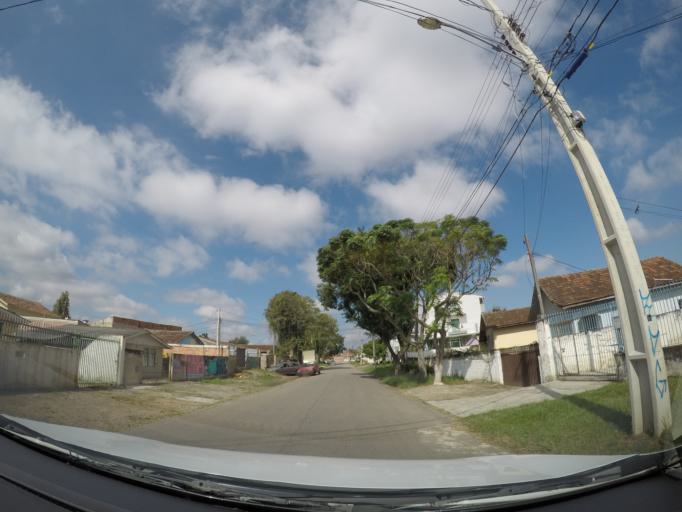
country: BR
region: Parana
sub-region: Sao Jose Dos Pinhais
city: Sao Jose dos Pinhais
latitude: -25.4949
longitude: -49.2228
